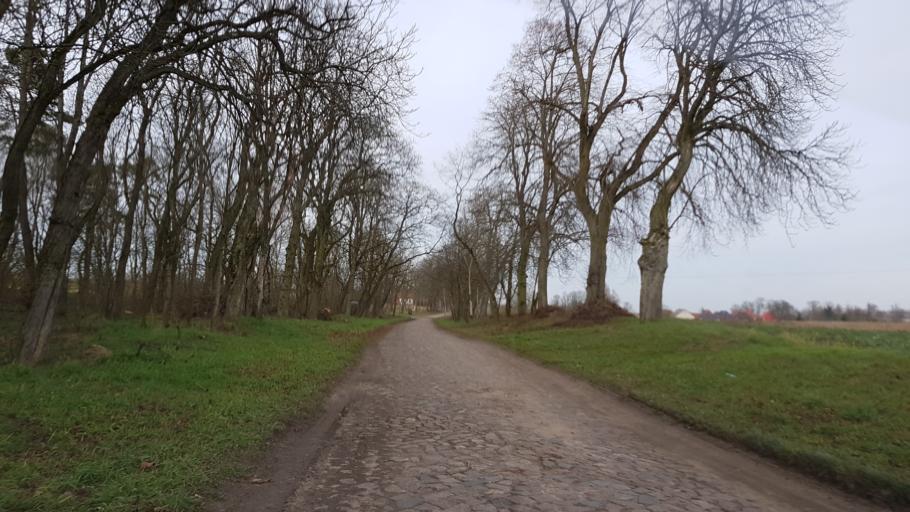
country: PL
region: Lubusz
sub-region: Powiat strzelecko-drezdenecki
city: Strzelce Krajenskie
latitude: 52.9265
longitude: 15.4168
